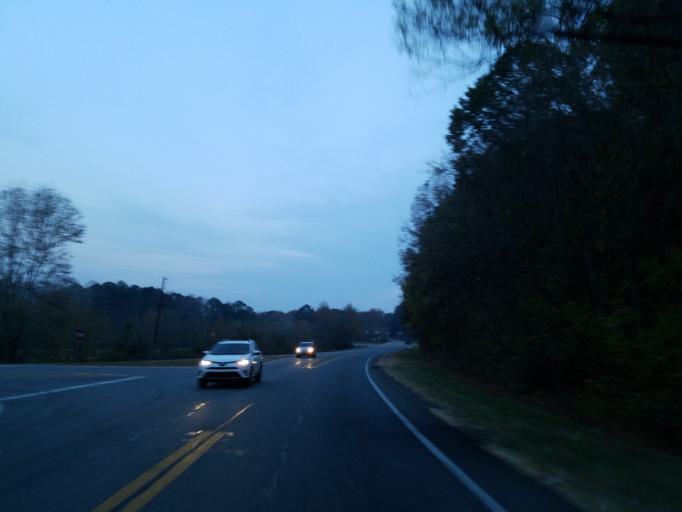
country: US
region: Georgia
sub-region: Pickens County
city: Jasper
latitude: 34.5200
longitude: -84.5240
